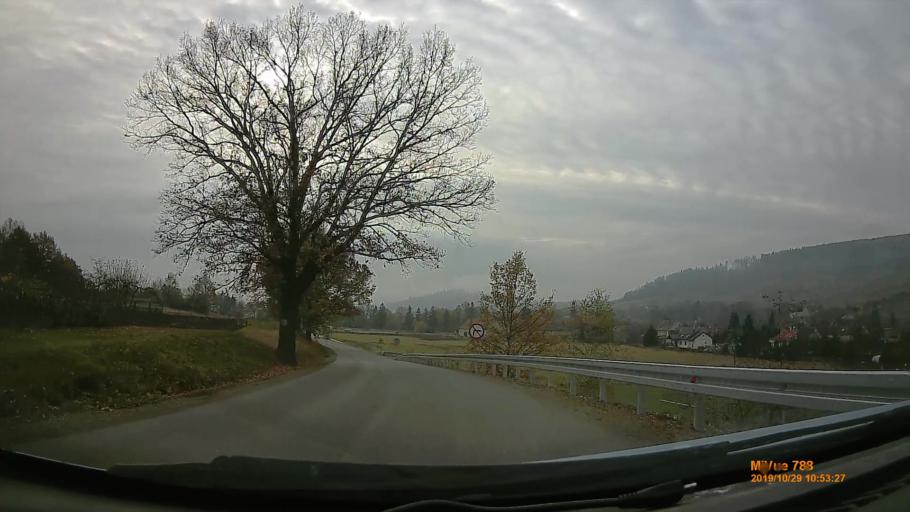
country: PL
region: Lower Silesian Voivodeship
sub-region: Powiat klodzki
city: Nowa Ruda
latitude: 50.5312
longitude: 16.4824
